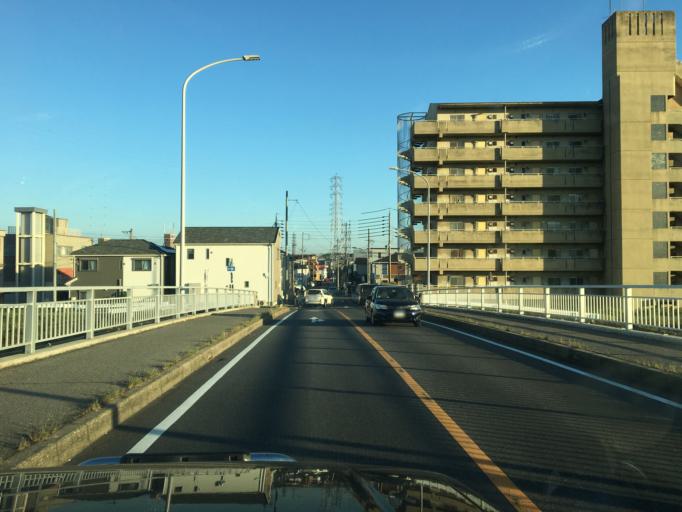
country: JP
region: Aichi
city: Kasugai
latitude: 35.1996
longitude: 137.0010
